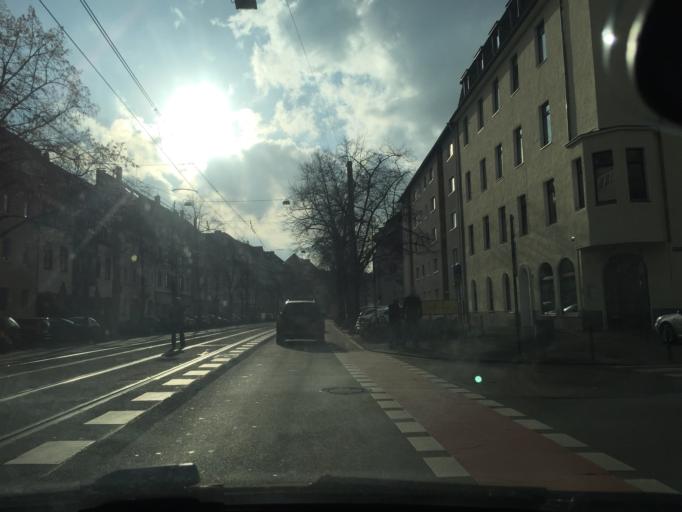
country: DE
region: North Rhine-Westphalia
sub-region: Regierungsbezirk Koln
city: Deutz
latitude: 50.9356
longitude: 6.9778
